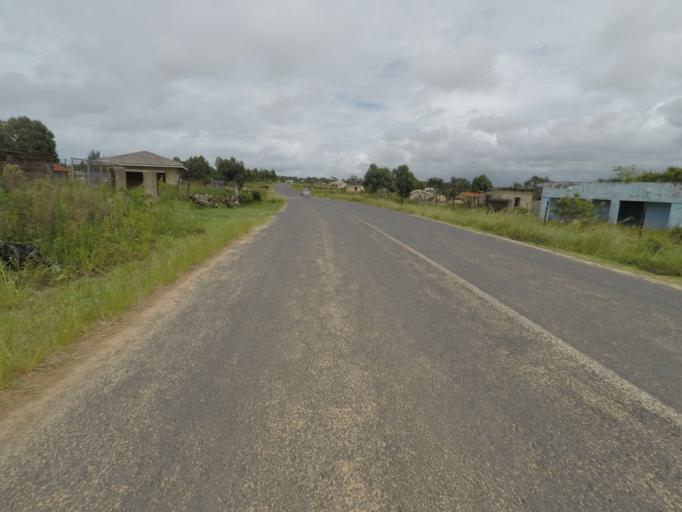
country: ZA
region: KwaZulu-Natal
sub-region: uThungulu District Municipality
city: eSikhawini
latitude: -28.9137
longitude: 31.8516
